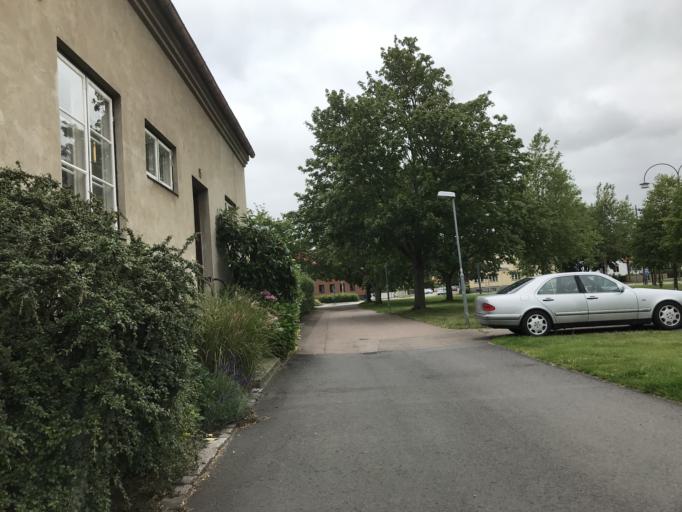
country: SE
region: Skane
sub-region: Landskrona
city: Landskrona
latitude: 55.8784
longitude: 12.8383
